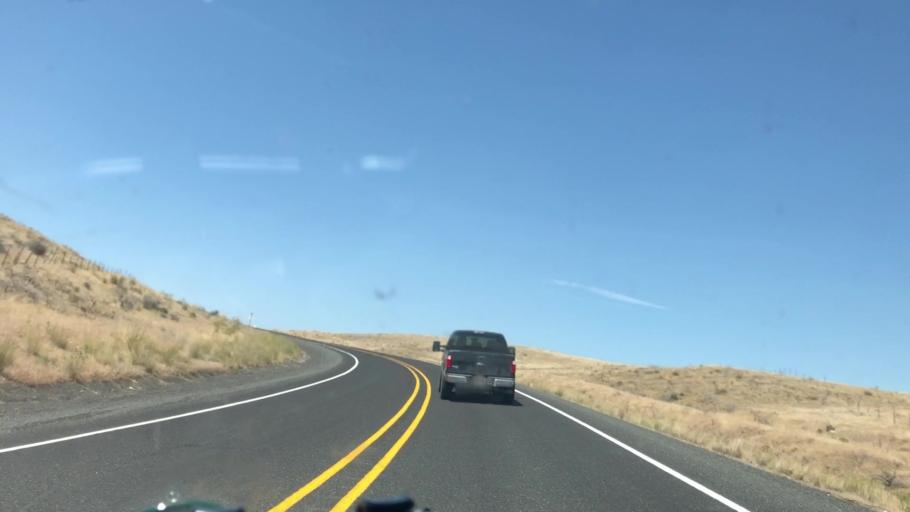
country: US
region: Idaho
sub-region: Owyhee County
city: Marsing
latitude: 43.2329
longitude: -117.0460
